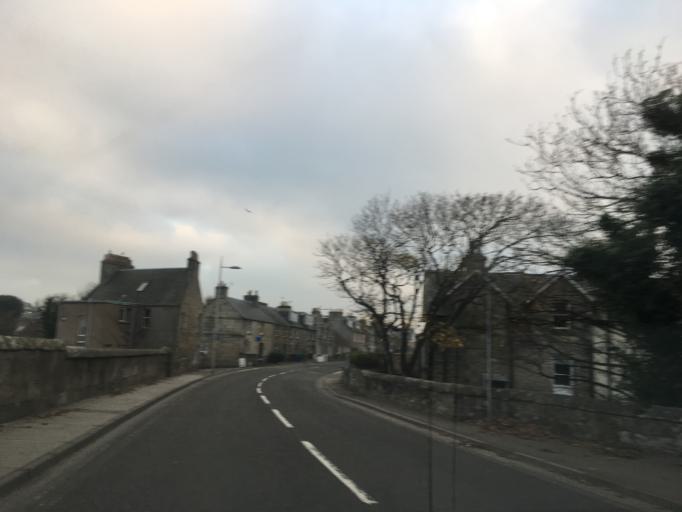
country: GB
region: Scotland
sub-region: Fife
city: Saint Andrews
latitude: 56.3364
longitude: -2.7846
